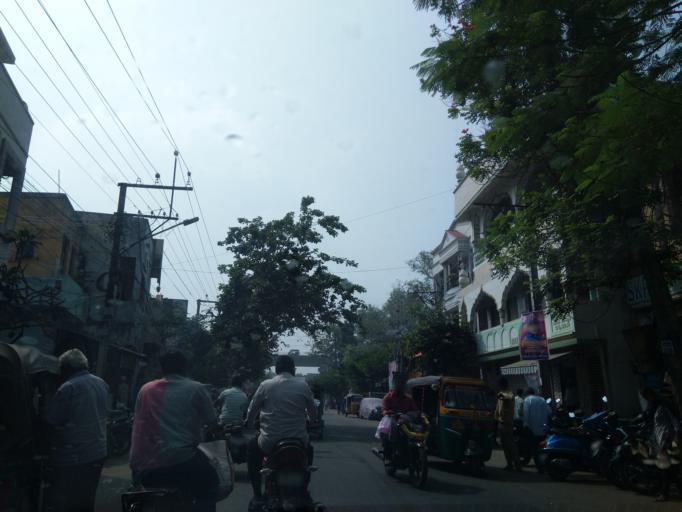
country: IN
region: Andhra Pradesh
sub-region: Krishna
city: Vijayawada
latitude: 16.5213
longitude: 80.6031
